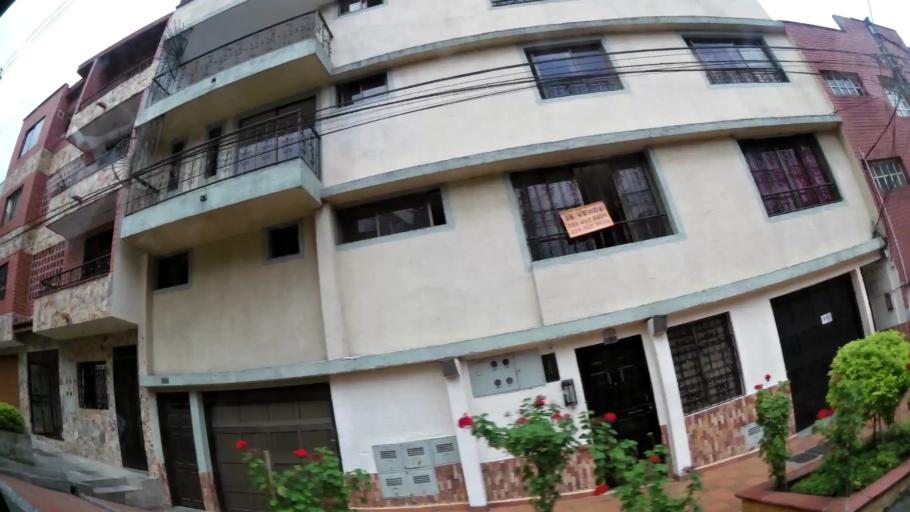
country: CO
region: Antioquia
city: Medellin
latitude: 6.2539
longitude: -75.5567
